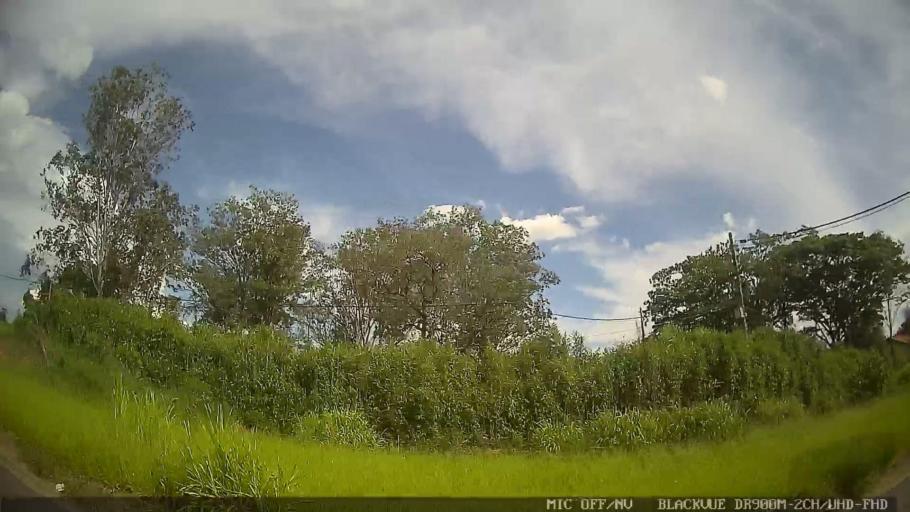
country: BR
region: Sao Paulo
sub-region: Conchas
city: Conchas
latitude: -23.0643
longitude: -47.9714
